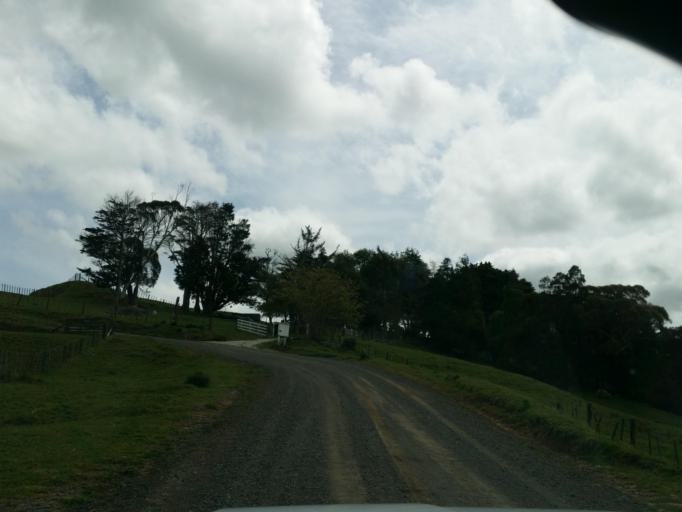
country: NZ
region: Northland
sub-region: Kaipara District
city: Dargaville
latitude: -35.9253
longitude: 174.0164
